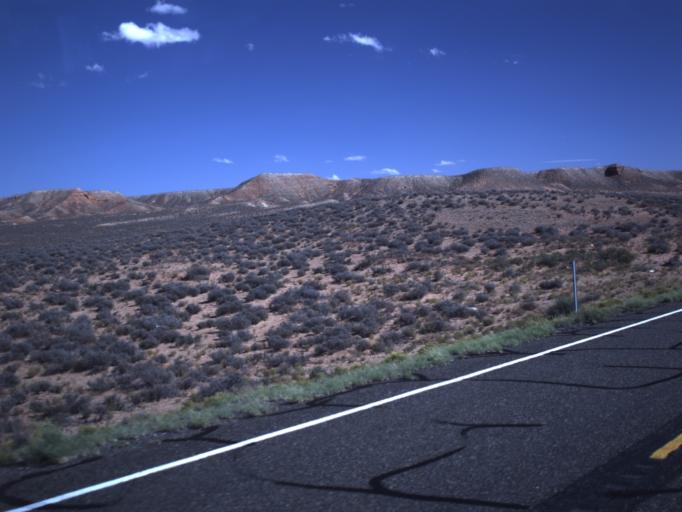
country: US
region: Utah
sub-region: Wayne County
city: Loa
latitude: 38.0947
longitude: -110.6202
